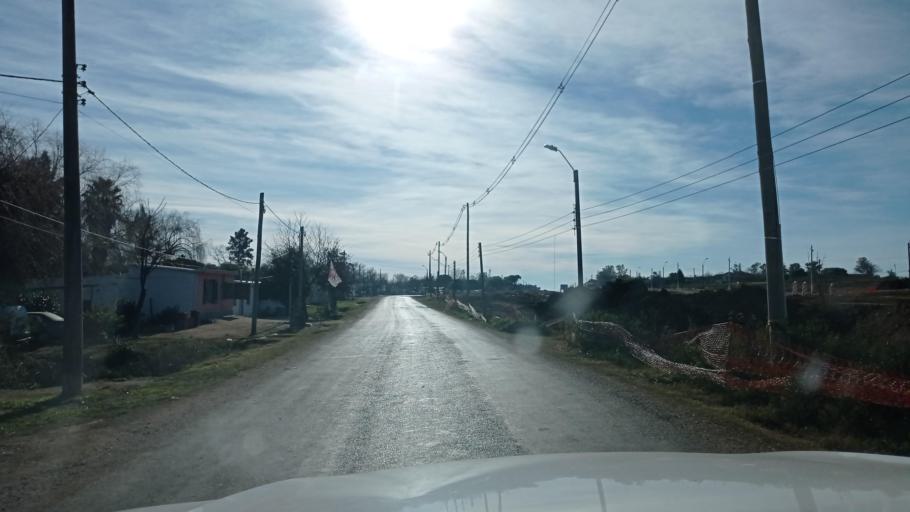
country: UY
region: Florida
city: Florida
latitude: -34.1035
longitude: -56.2423
